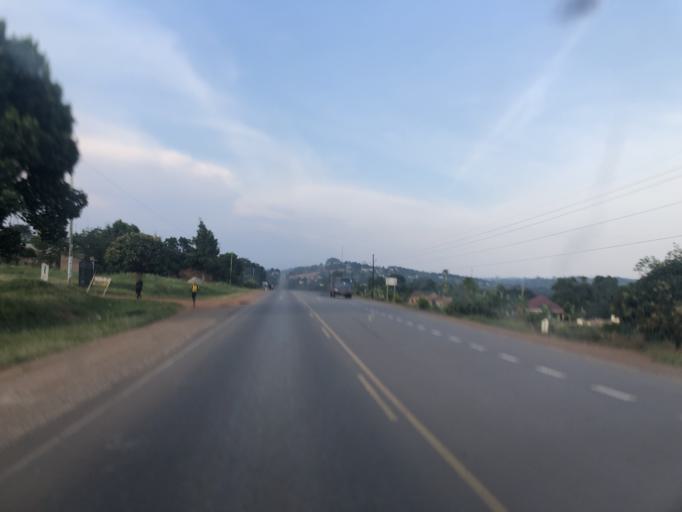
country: UG
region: Central Region
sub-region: Mpigi District
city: Mpigi
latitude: 0.2097
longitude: 32.3189
